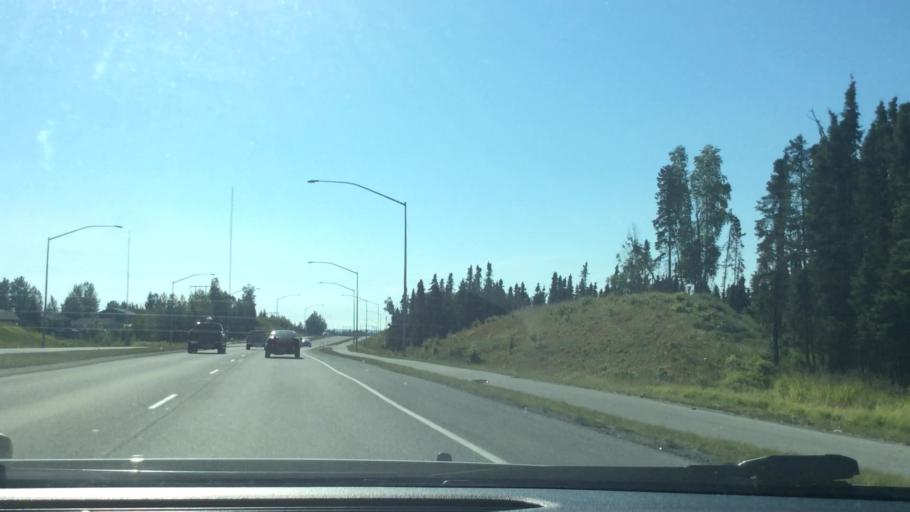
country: US
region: Alaska
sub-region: Anchorage Municipality
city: Anchorage
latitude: 61.1669
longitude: -149.8154
